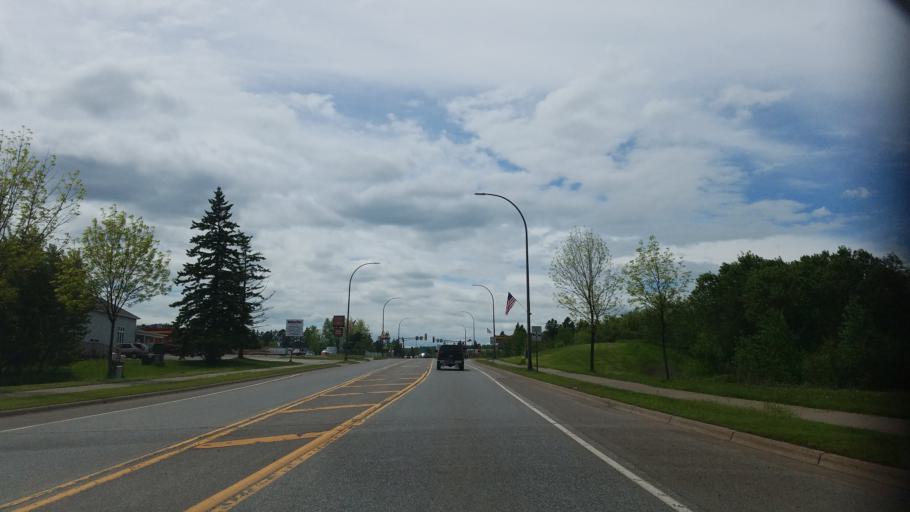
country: US
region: Minnesota
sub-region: Lake County
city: Two Harbors
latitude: 47.0257
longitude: -91.6777
